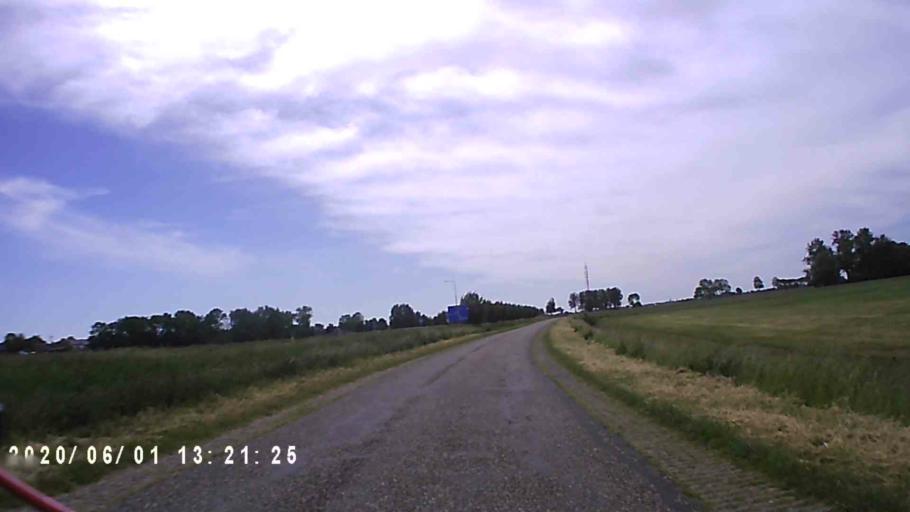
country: NL
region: Friesland
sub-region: Gemeente Littenseradiel
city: Wommels
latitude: 53.1119
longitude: 5.5836
